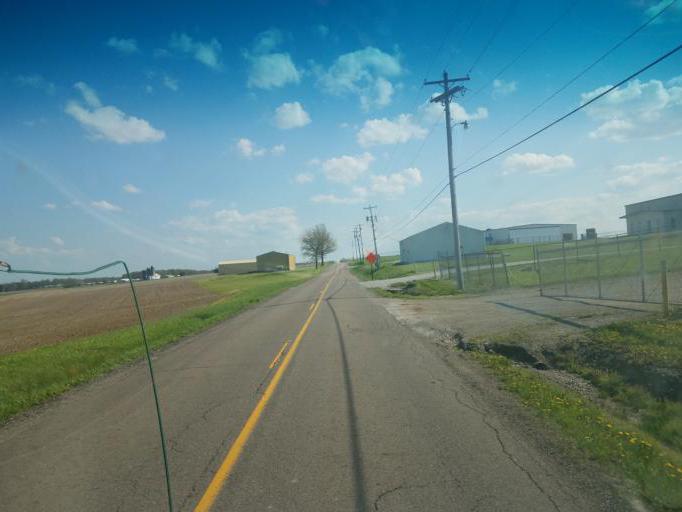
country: US
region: Ohio
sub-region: Wayne County
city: Smithville
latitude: 40.8782
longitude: -81.8782
